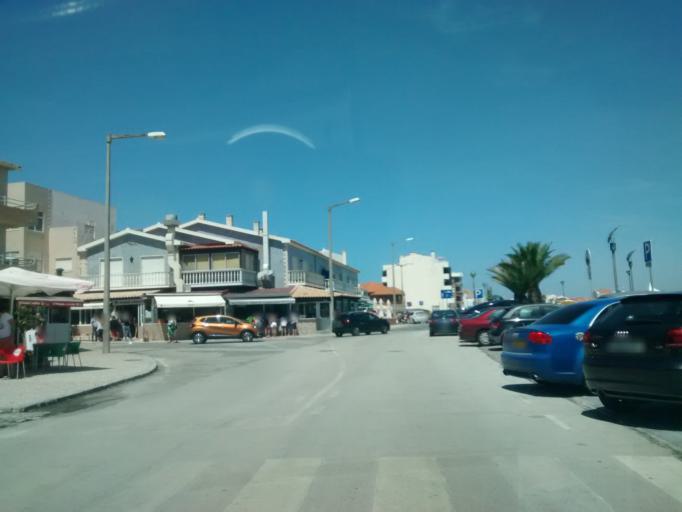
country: PT
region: Coimbra
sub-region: Mira
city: Mira
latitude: 40.4515
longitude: -8.8018
